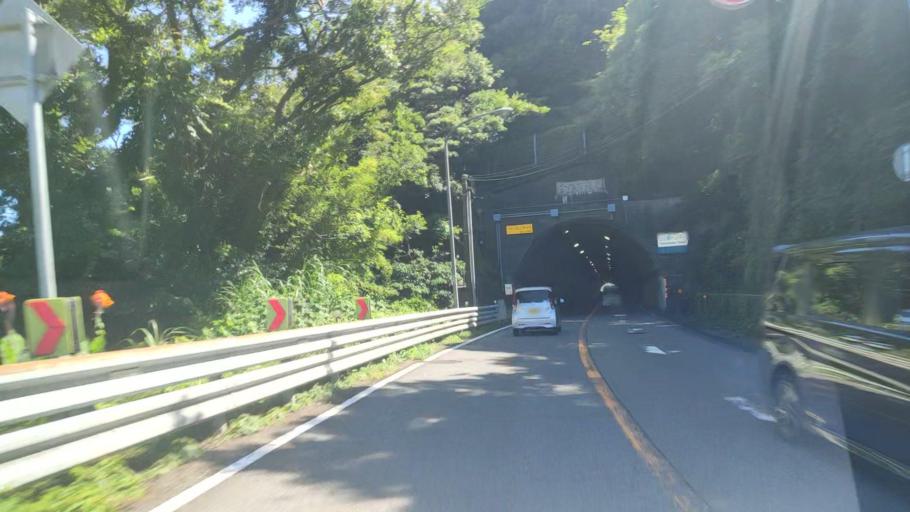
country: JP
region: Wakayama
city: Shingu
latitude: 33.5762
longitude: 135.9187
